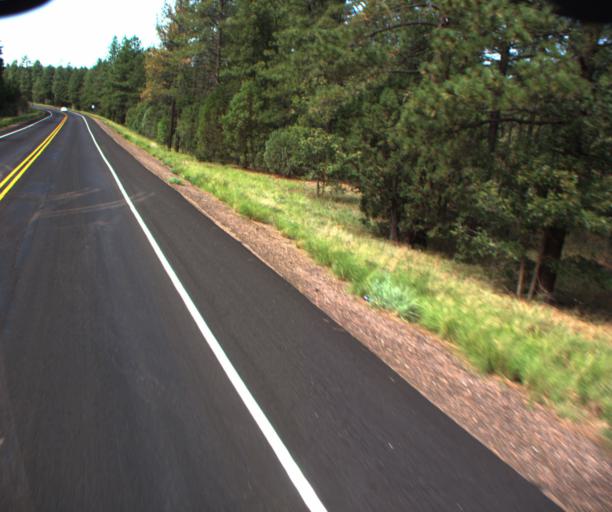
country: US
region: Arizona
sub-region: Navajo County
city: Show Low
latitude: 34.1959
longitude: -110.0884
